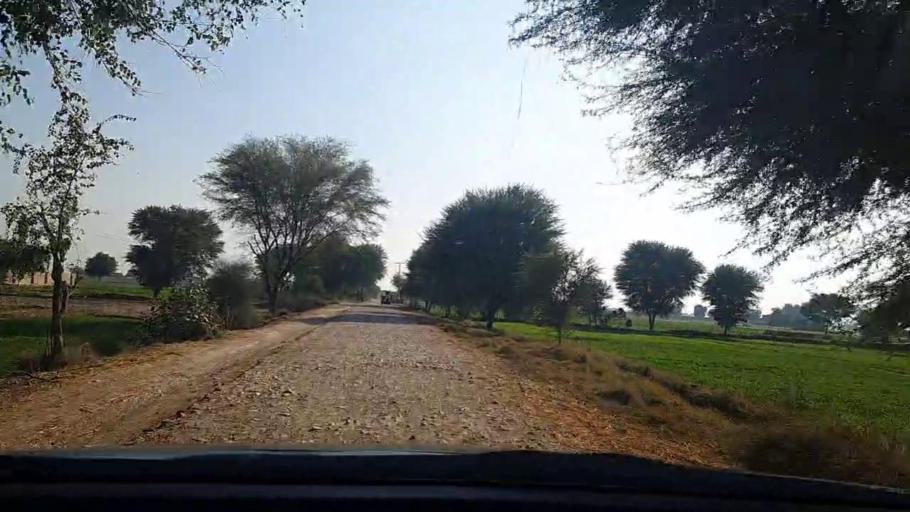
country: PK
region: Sindh
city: Sehwan
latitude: 26.3187
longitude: 68.0062
